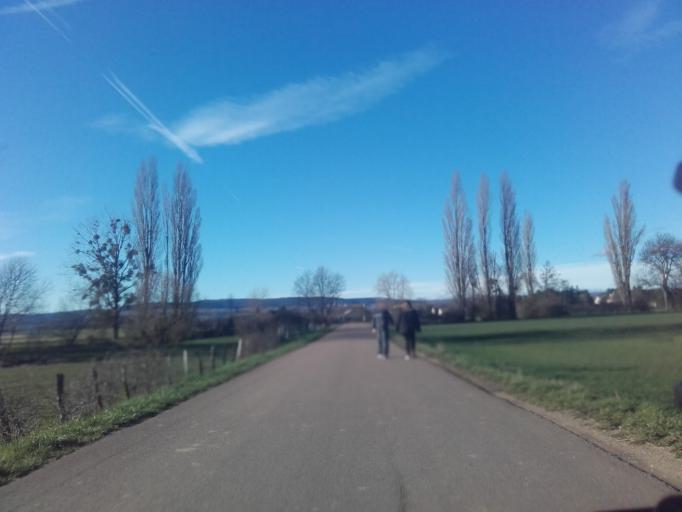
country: FR
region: Bourgogne
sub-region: Departement de la Cote-d'Or
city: Corpeau
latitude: 46.9248
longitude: 4.7888
